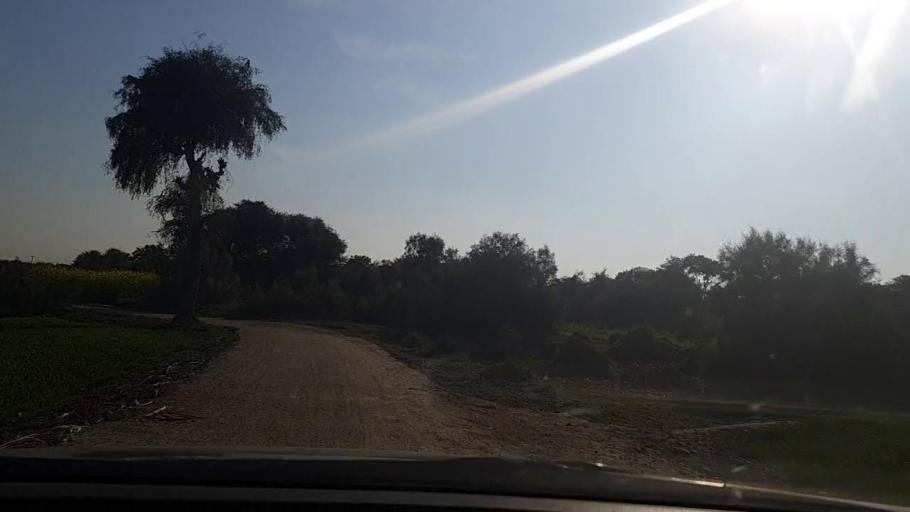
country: PK
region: Sindh
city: Sehwan
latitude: 26.3003
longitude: 68.0043
